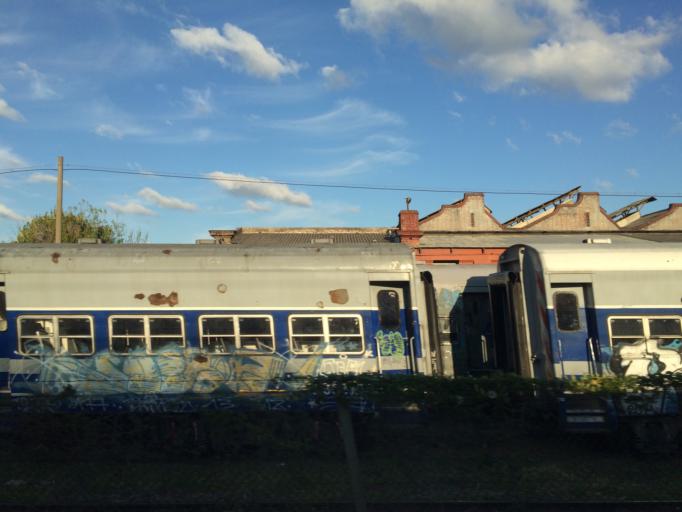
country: AR
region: Buenos Aires
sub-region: Partido de Lanus
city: Lanus
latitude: -34.7240
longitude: -58.3932
